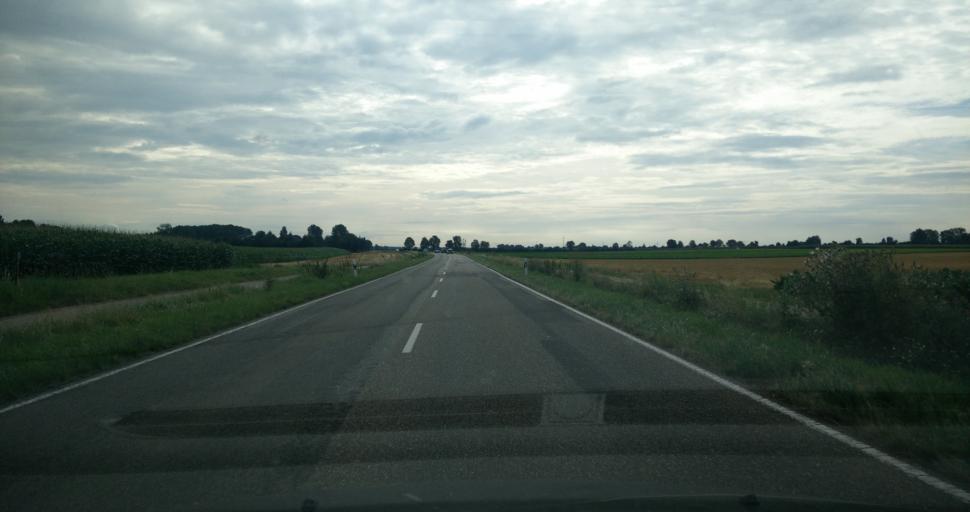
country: DE
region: Rheinland-Pfalz
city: Minfeld
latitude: 49.0926
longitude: 8.1467
